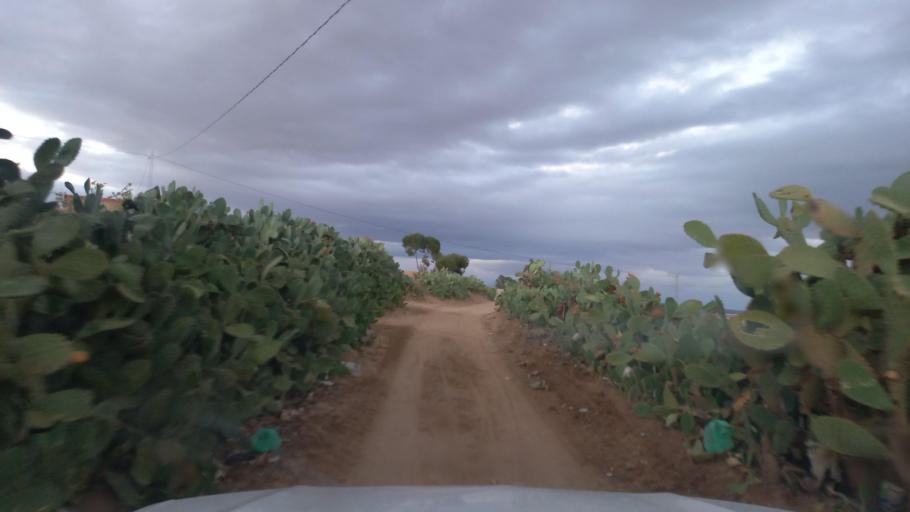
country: TN
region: Al Qasrayn
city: Kasserine
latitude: 35.2561
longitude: 8.9370
